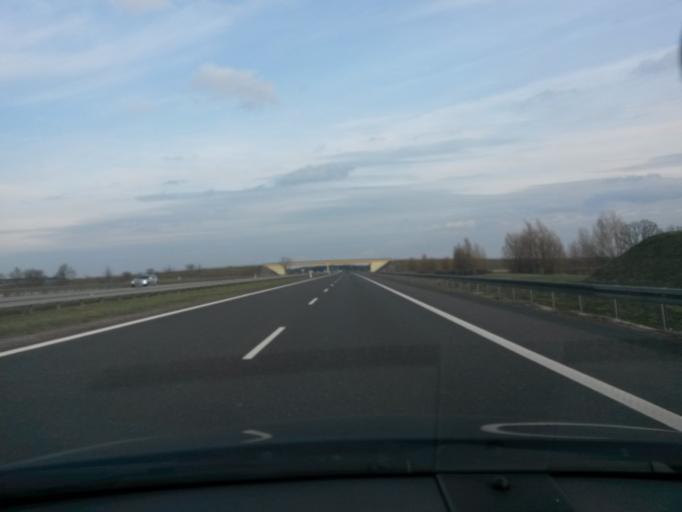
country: PL
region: Lodz Voivodeship
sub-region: Powiat poddebicki
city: Dalikow
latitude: 51.9615
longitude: 19.1210
